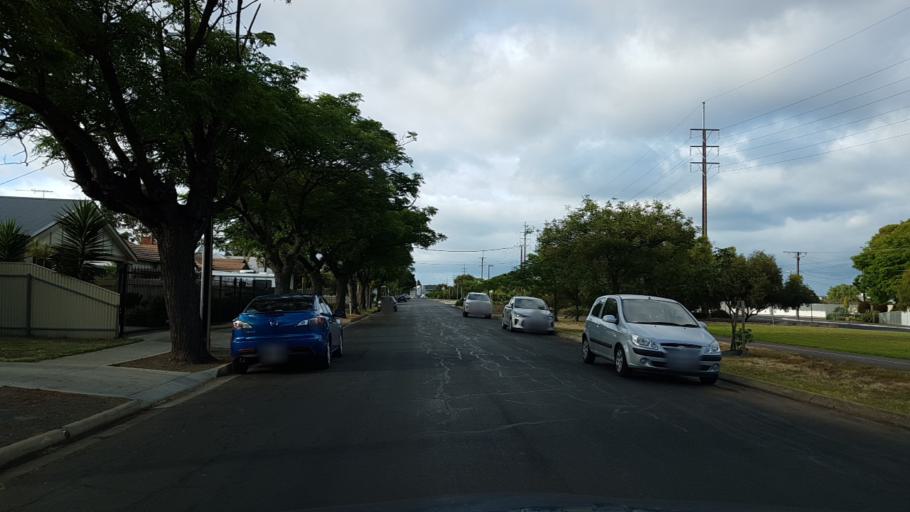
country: AU
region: South Australia
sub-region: Unley
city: Forestville
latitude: -34.9441
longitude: 138.5671
